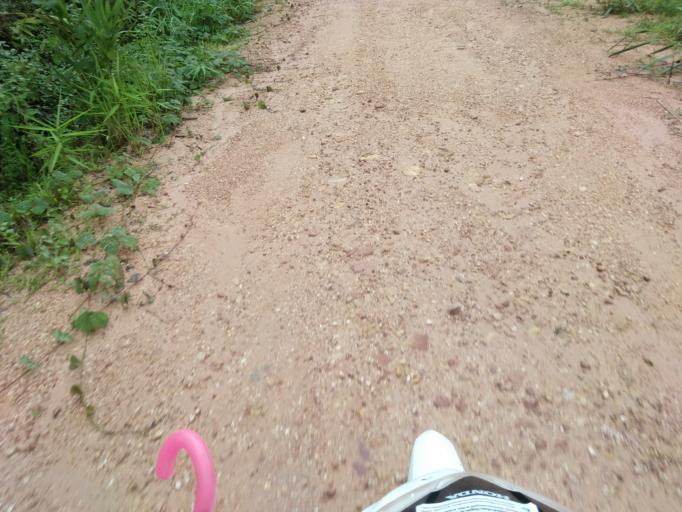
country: TH
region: Nan
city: Chaloem Phra Kiat
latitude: 19.7578
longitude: 100.7420
